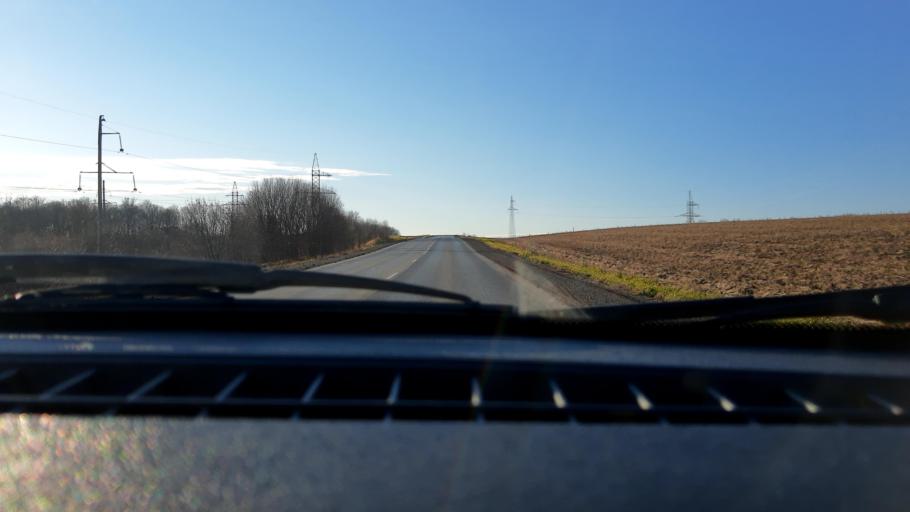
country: RU
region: Bashkortostan
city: Mikhaylovka
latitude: 54.8308
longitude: 55.8952
